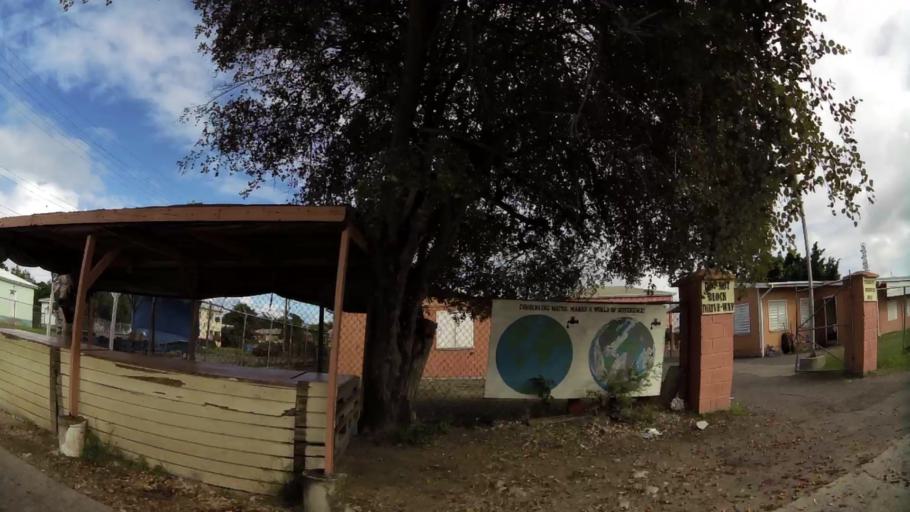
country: AG
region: Saint George
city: Piggotts
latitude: 17.1283
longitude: -61.8226
